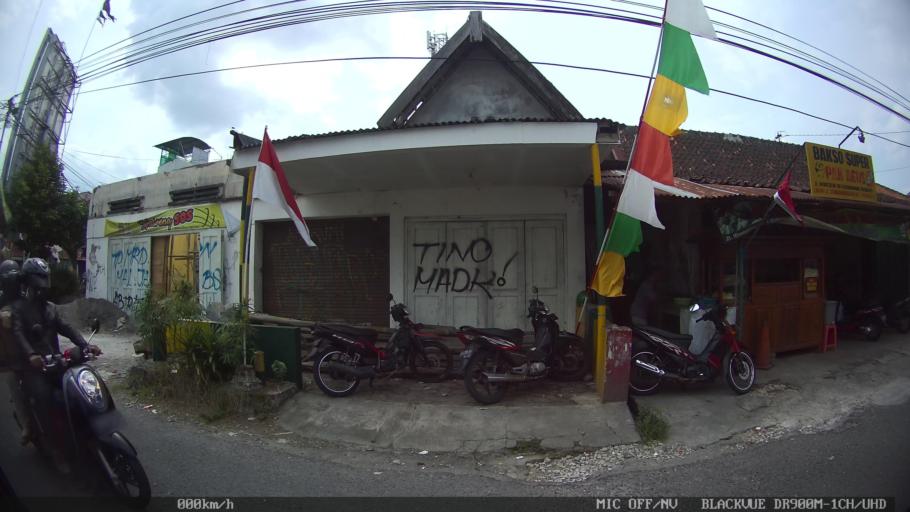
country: ID
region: Daerah Istimewa Yogyakarta
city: Yogyakarta
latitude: -7.8023
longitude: 110.4026
